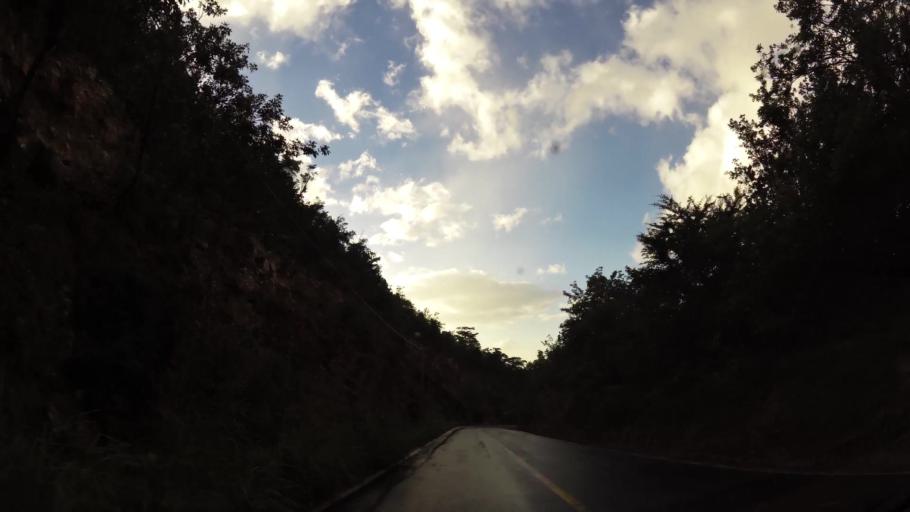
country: DM
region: Saint Peter
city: Colihaut
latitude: 15.5281
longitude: -61.4671
